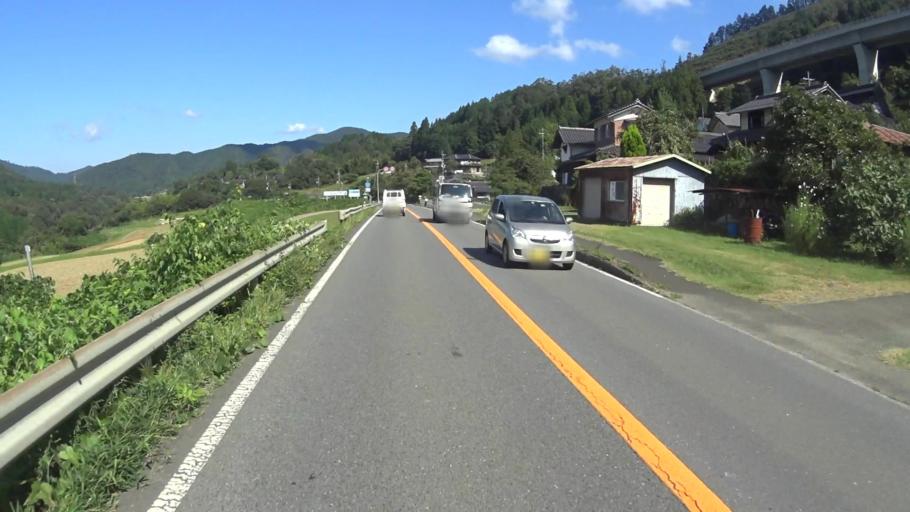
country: JP
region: Kyoto
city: Ayabe
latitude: 35.2862
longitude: 135.3357
